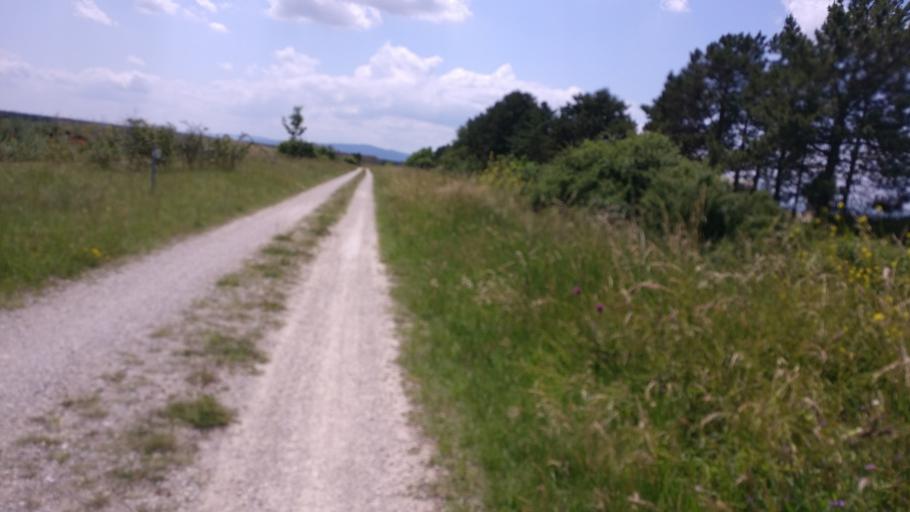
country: AT
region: Lower Austria
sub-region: Politischer Bezirk Wiener Neustadt
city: Sollenau
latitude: 47.8740
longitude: 16.2813
